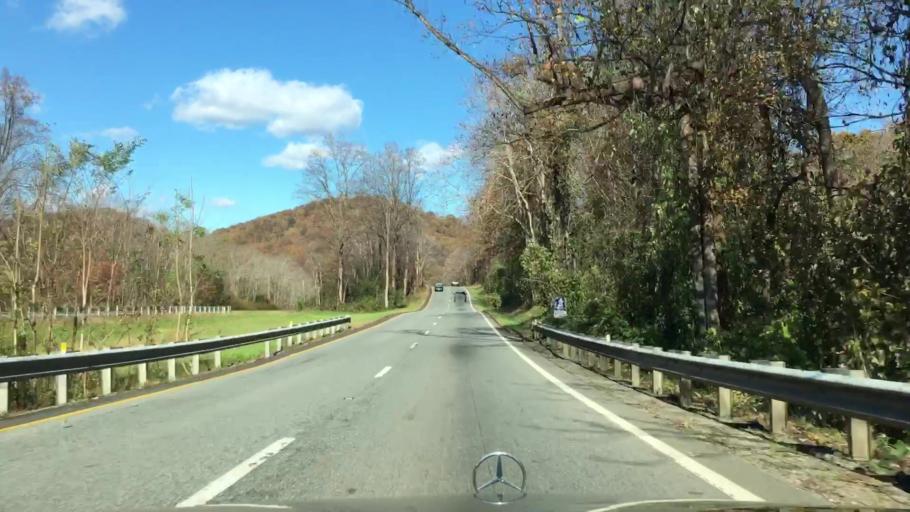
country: US
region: Virginia
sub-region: Nelson County
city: Nellysford
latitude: 37.8784
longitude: -78.7147
